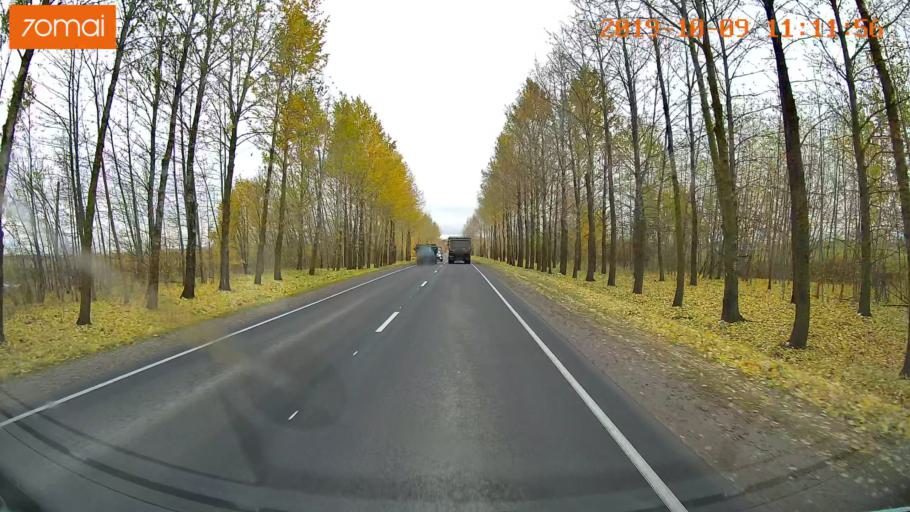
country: RU
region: Vologda
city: Vologda
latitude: 59.1728
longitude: 39.8251
